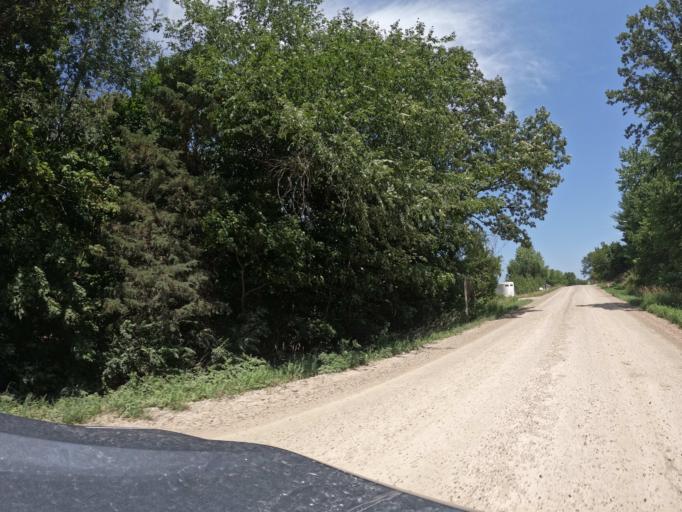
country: US
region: Iowa
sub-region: Henry County
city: Mount Pleasant
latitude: 40.9376
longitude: -91.5809
